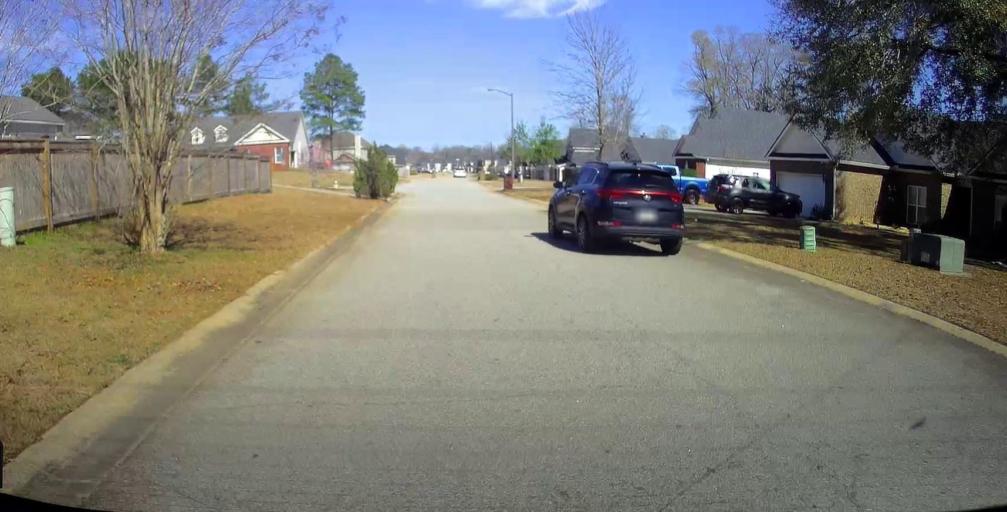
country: US
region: Georgia
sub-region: Houston County
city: Perry
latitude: 32.5005
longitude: -83.6488
